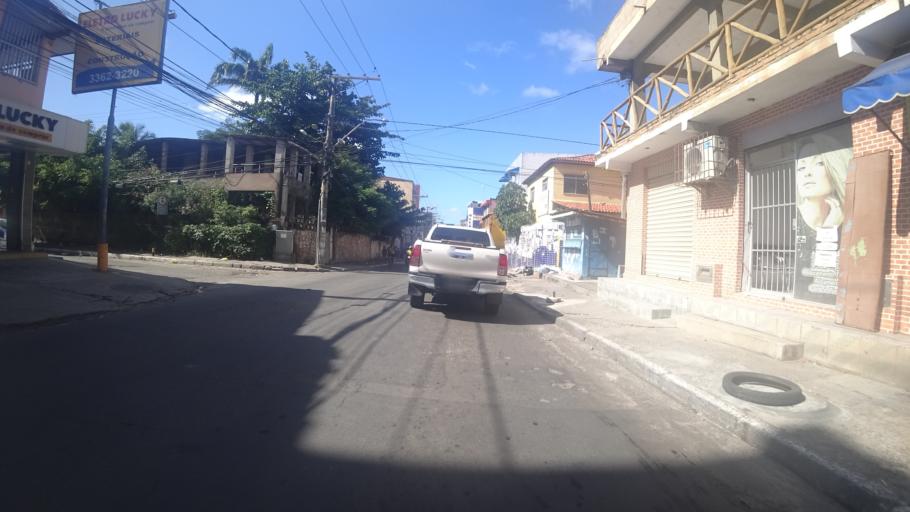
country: BR
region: Bahia
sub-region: Salvador
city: Salvador
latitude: -12.9763
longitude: -38.4307
